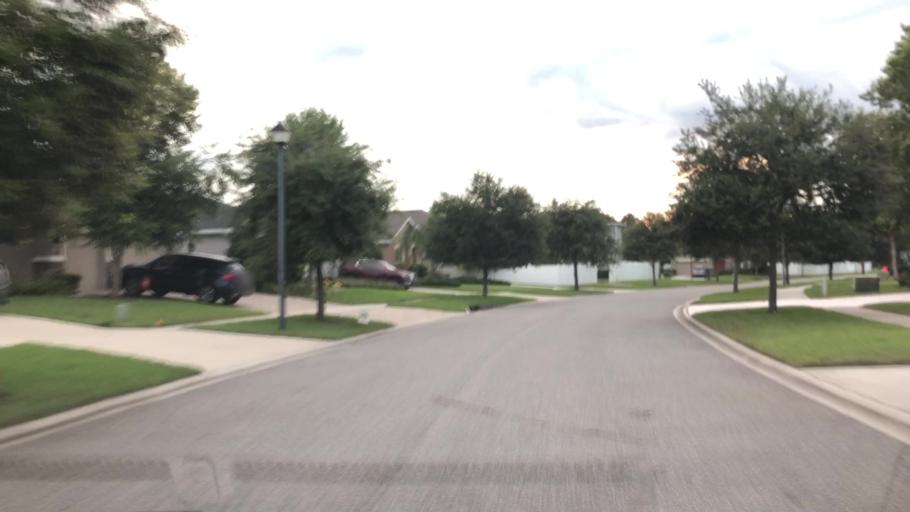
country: US
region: Florida
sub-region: Saint Johns County
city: Palm Valley
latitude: 30.1020
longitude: -81.4596
